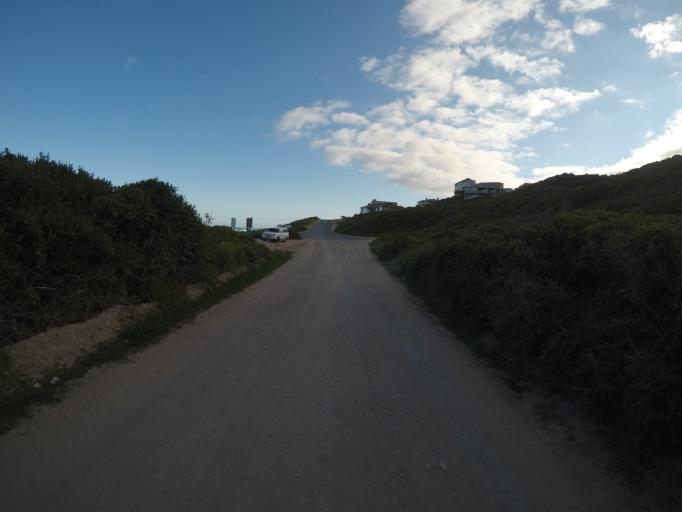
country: ZA
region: Western Cape
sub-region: Eden District Municipality
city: Riversdale
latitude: -34.4196
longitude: 21.3509
